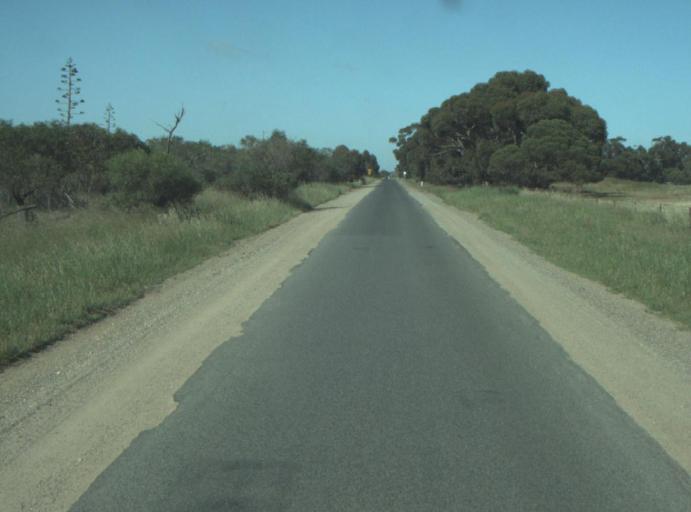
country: AU
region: Victoria
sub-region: Greater Geelong
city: Lara
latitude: -37.9970
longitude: 144.4465
